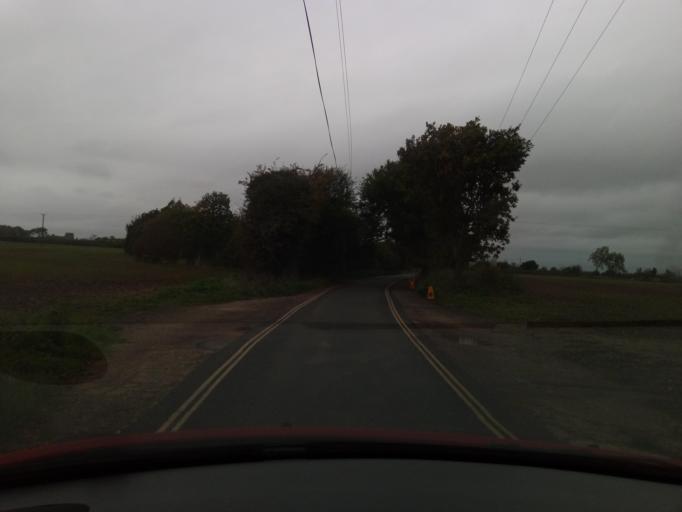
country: GB
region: England
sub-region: Essex
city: Brightlingsea
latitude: 51.7934
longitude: 0.9886
